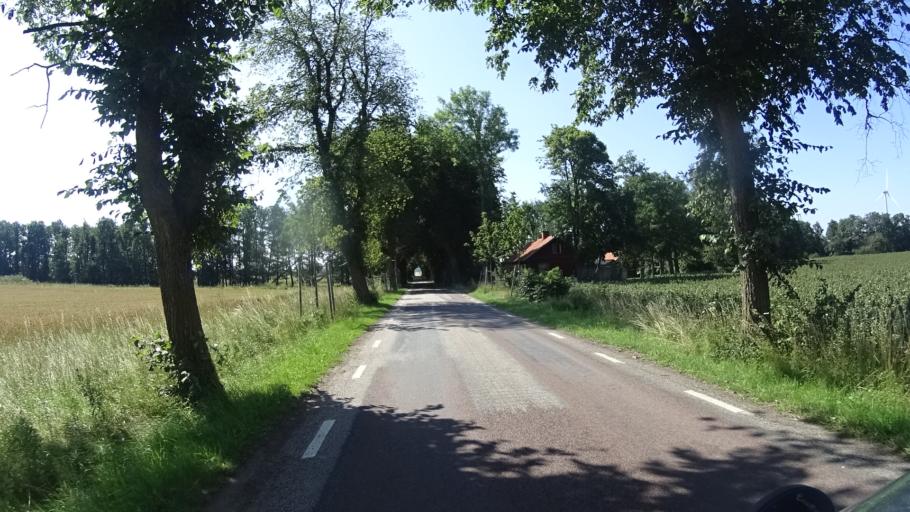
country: SE
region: OEstergoetland
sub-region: Vadstena Kommun
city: Herrestad
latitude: 58.3201
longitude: 14.8420
